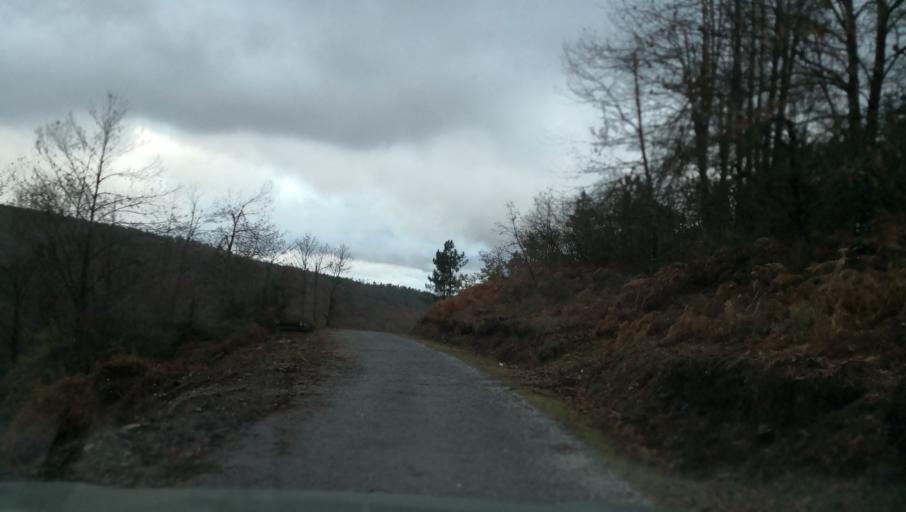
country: PT
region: Vila Real
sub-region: Santa Marta de Penaguiao
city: Santa Marta de Penaguiao
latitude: 41.3117
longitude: -7.8673
